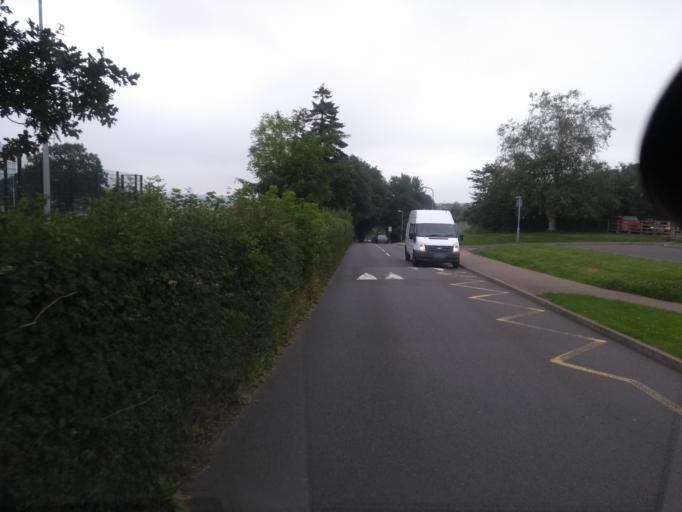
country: GB
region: England
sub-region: Devon
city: Axminster
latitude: 50.7827
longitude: -2.9923
